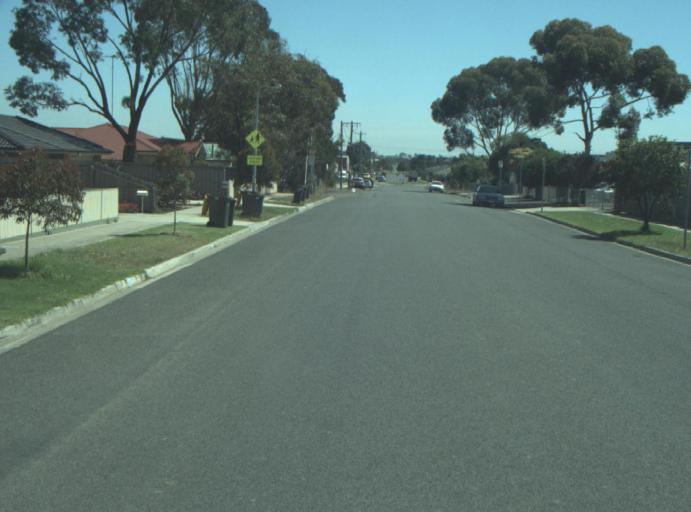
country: AU
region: Victoria
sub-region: Greater Geelong
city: Breakwater
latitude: -38.1986
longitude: 144.3473
